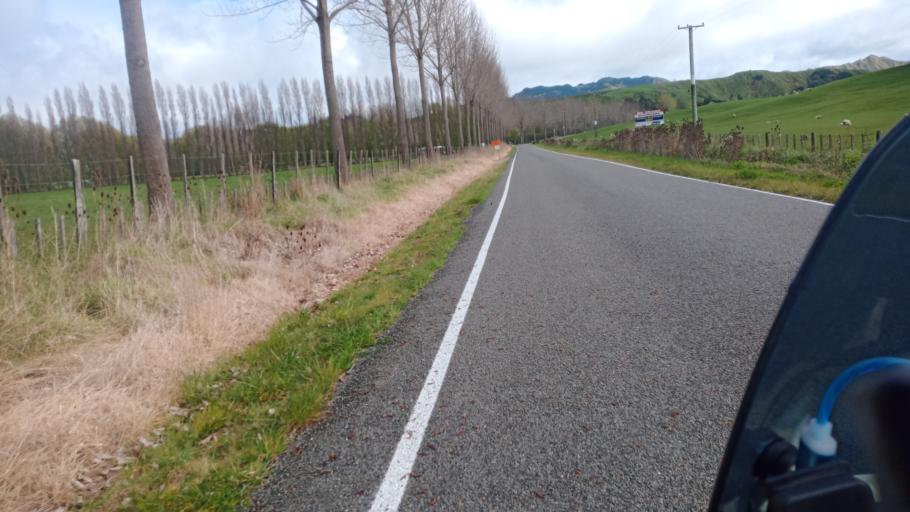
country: NZ
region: Gisborne
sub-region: Gisborne District
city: Gisborne
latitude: -38.5790
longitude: 178.1799
